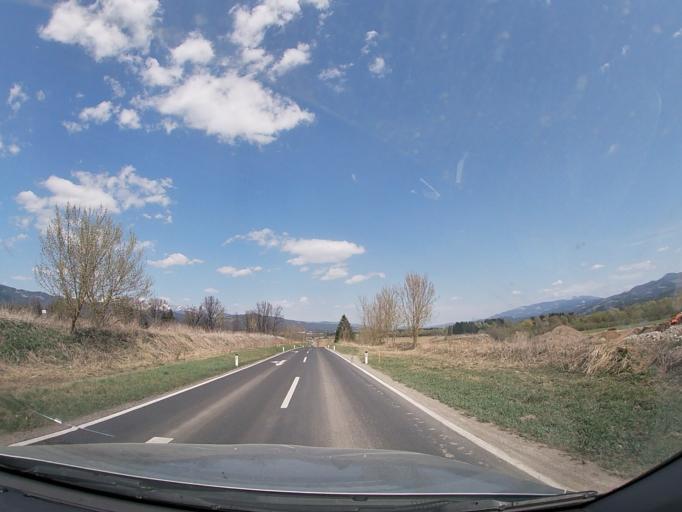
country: AT
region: Styria
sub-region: Politischer Bezirk Murtal
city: Zeltweg
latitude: 47.1730
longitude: 14.7481
